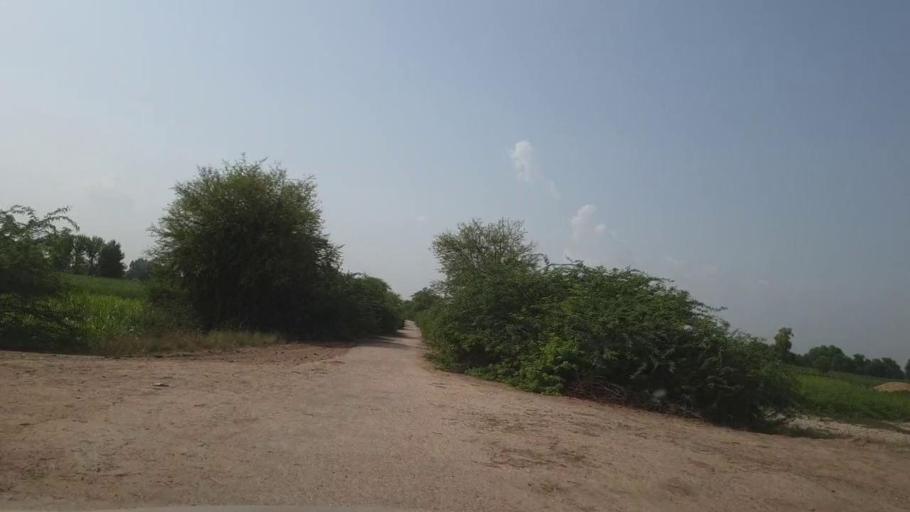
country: PK
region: Sindh
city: Pano Aqil
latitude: 27.7707
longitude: 69.1660
